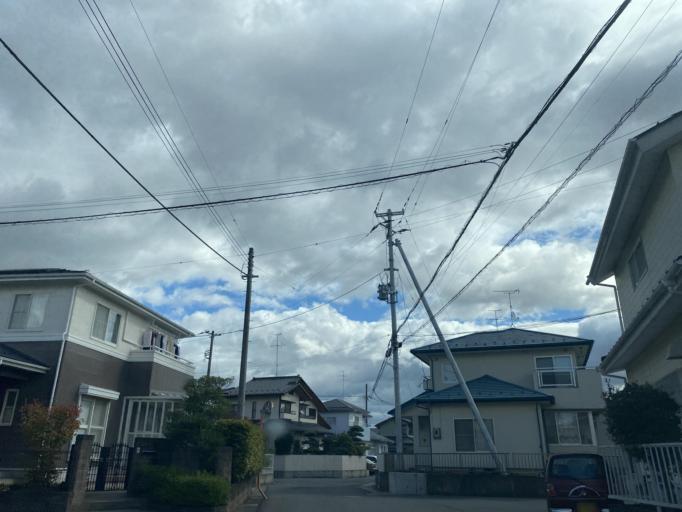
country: JP
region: Fukushima
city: Koriyama
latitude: 37.3829
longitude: 140.3413
